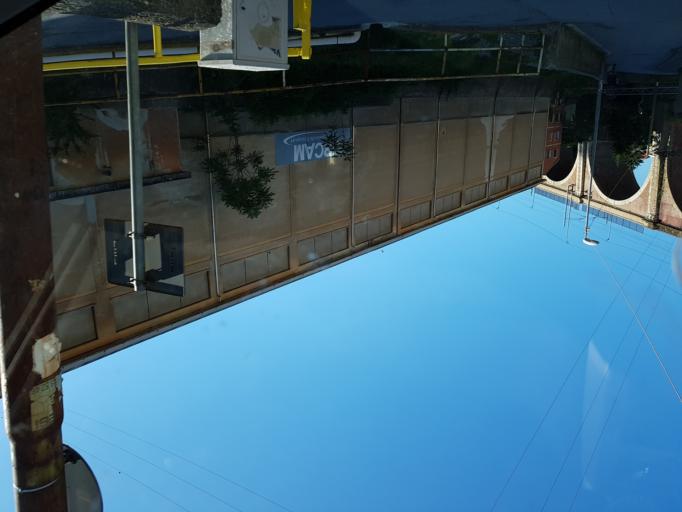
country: IT
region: Liguria
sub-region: Provincia di Genova
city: Genoa
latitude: 44.4544
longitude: 8.8897
